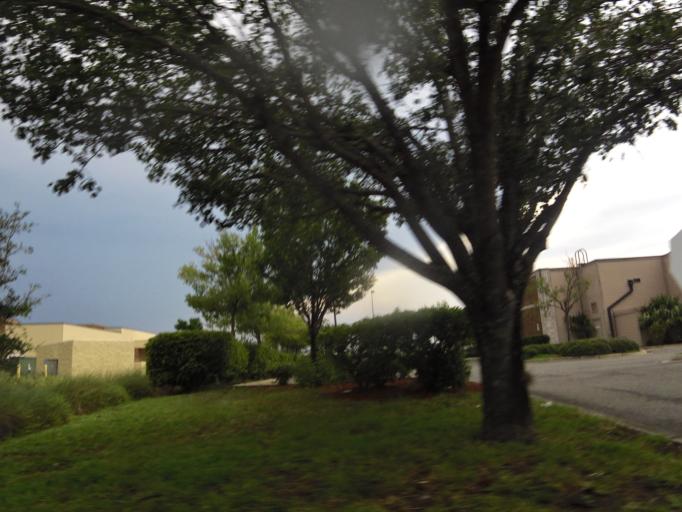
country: US
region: Florida
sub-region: Duval County
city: Atlantic Beach
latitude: 30.3192
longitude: -81.4933
